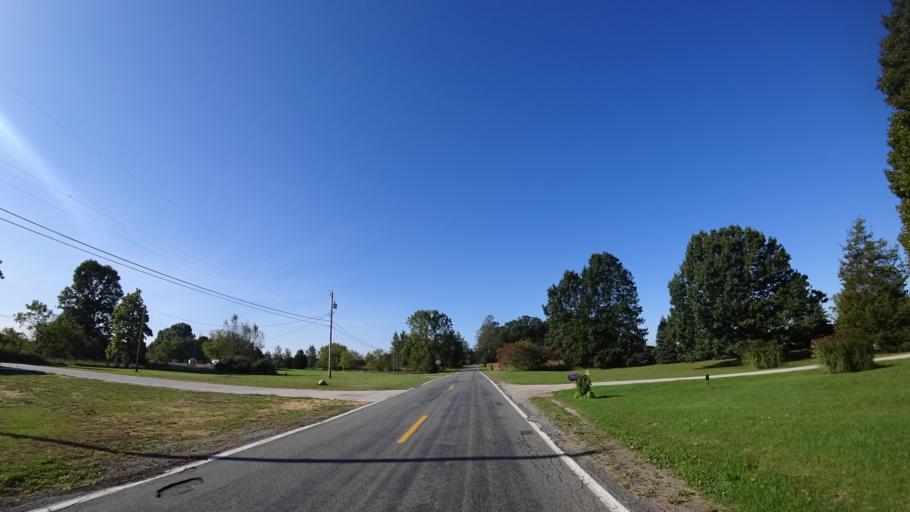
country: US
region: Michigan
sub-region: Berrien County
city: Benton Heights
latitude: 42.1710
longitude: -86.3922
